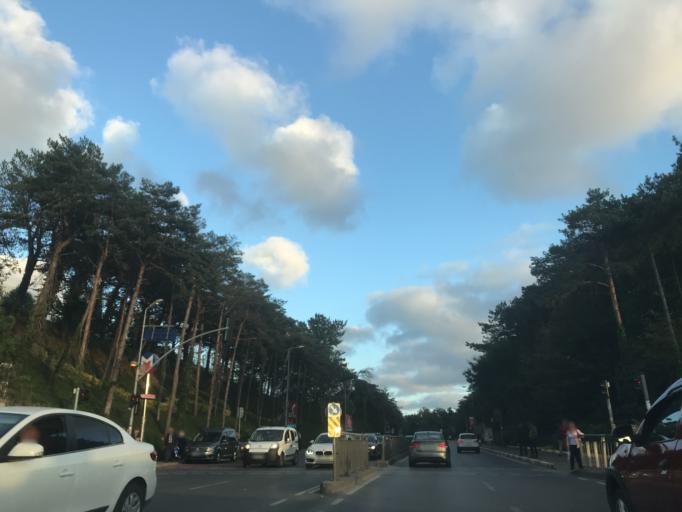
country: TR
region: Istanbul
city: Sisli
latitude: 41.1400
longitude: 29.0309
